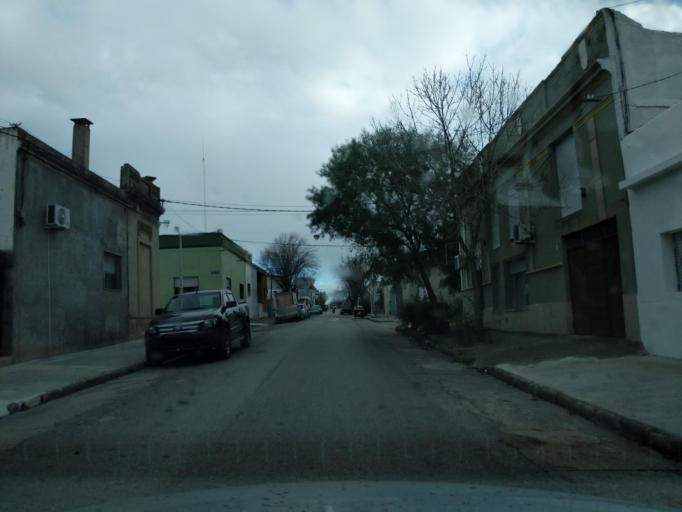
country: UY
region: Florida
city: Florida
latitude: -34.0937
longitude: -56.2115
